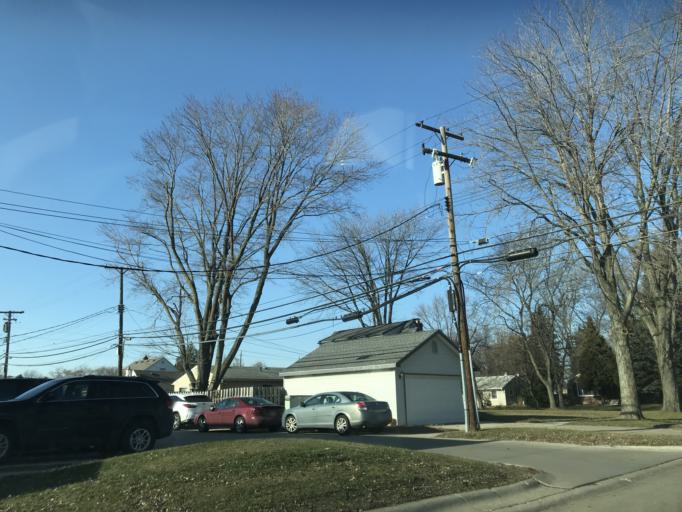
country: US
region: Michigan
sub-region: Oakland County
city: Madison Heights
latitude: 42.4909
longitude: -83.1147
